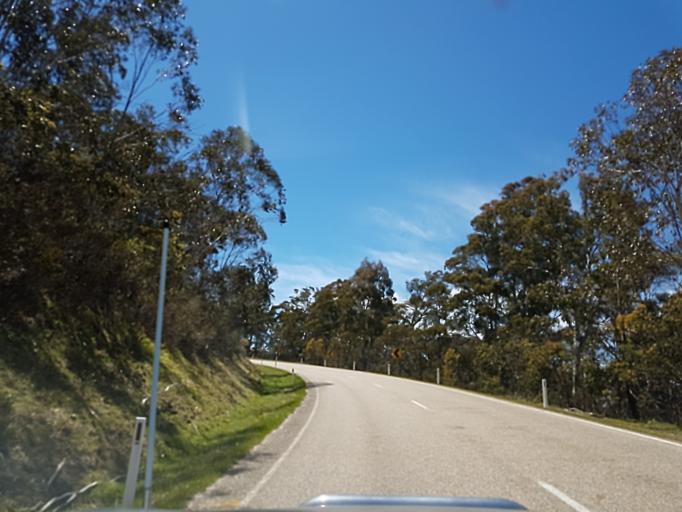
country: AU
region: Victoria
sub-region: Alpine
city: Mount Beauty
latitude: -37.0897
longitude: 147.3828
